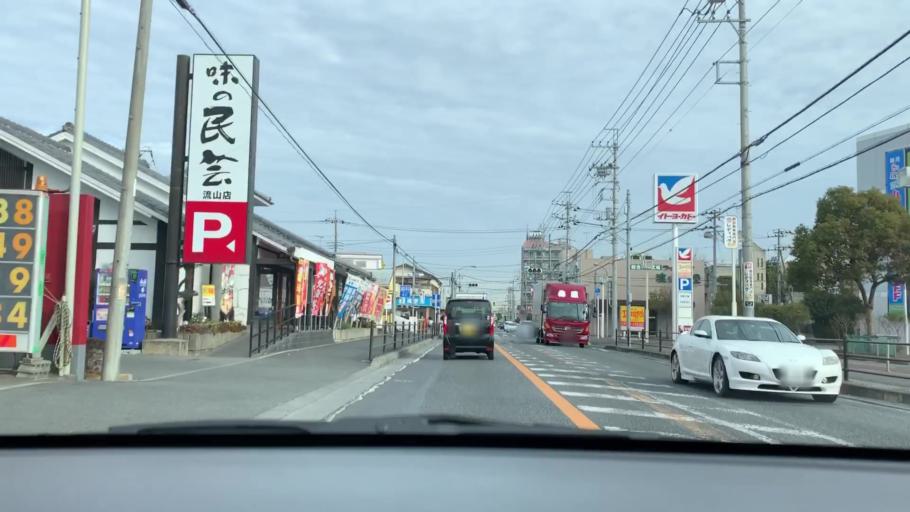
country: JP
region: Chiba
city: Nagareyama
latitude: 35.8499
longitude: 139.8982
